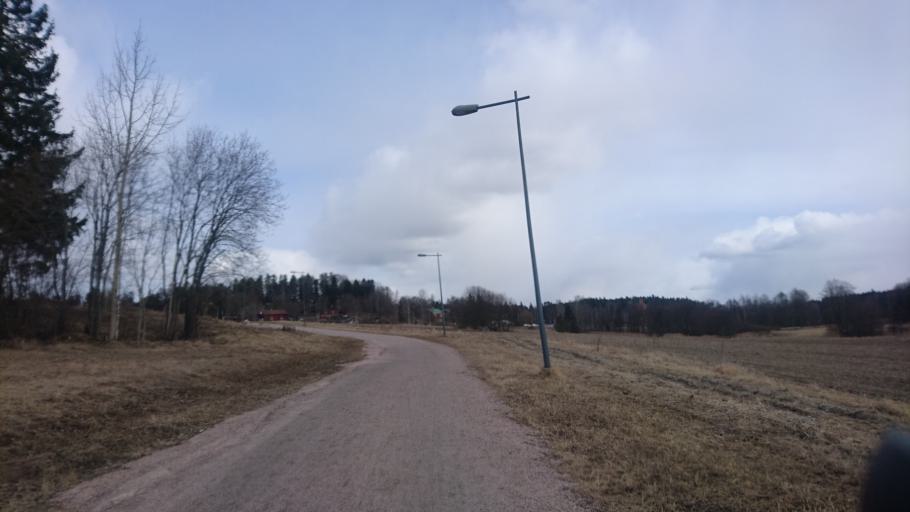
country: FI
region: Uusimaa
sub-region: Helsinki
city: Espoo
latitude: 60.2202
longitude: 24.6733
